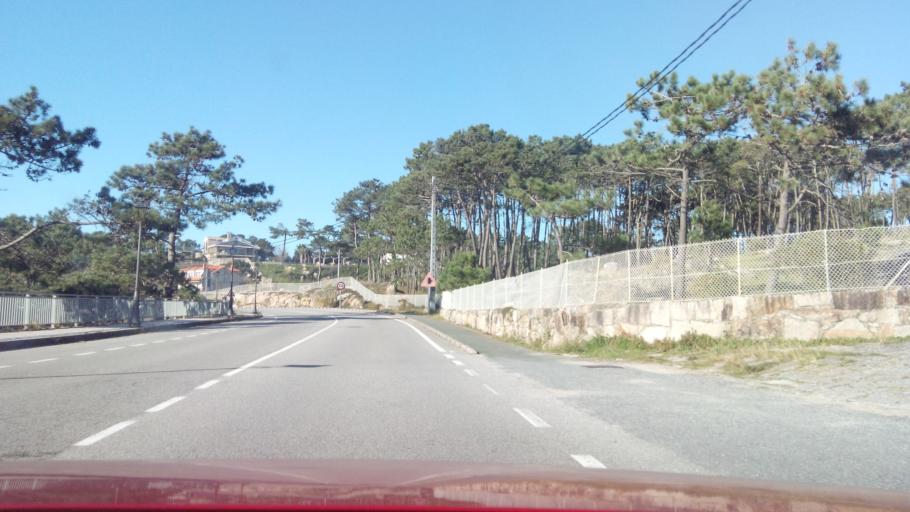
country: ES
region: Galicia
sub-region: Provincia de Pontevedra
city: O Grove
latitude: 42.4580
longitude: -8.8852
